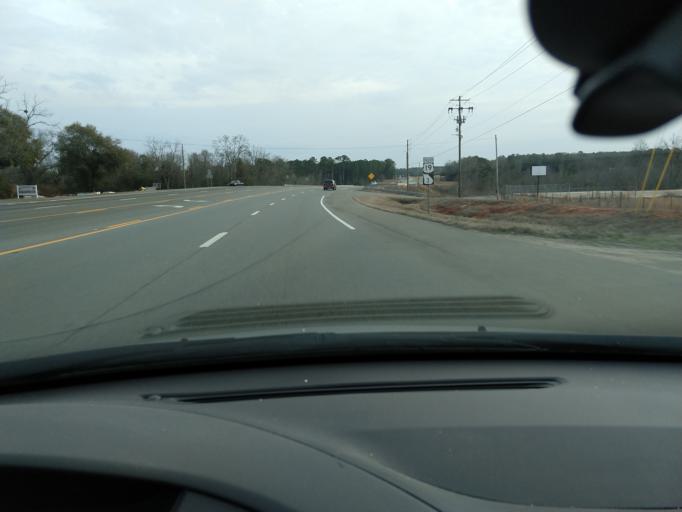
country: US
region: Georgia
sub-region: Sumter County
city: Americus
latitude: 32.0634
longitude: -84.2526
